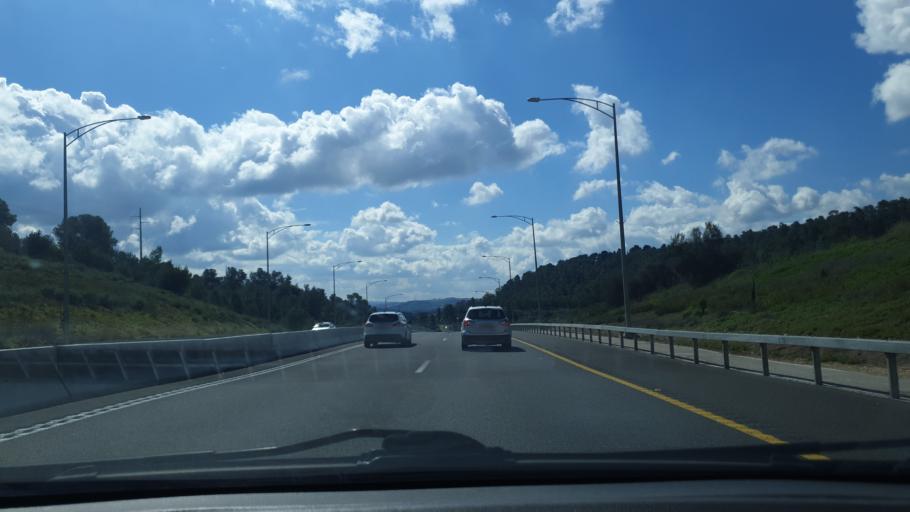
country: IL
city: Mevo horon
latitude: 31.7938
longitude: 35.0145
